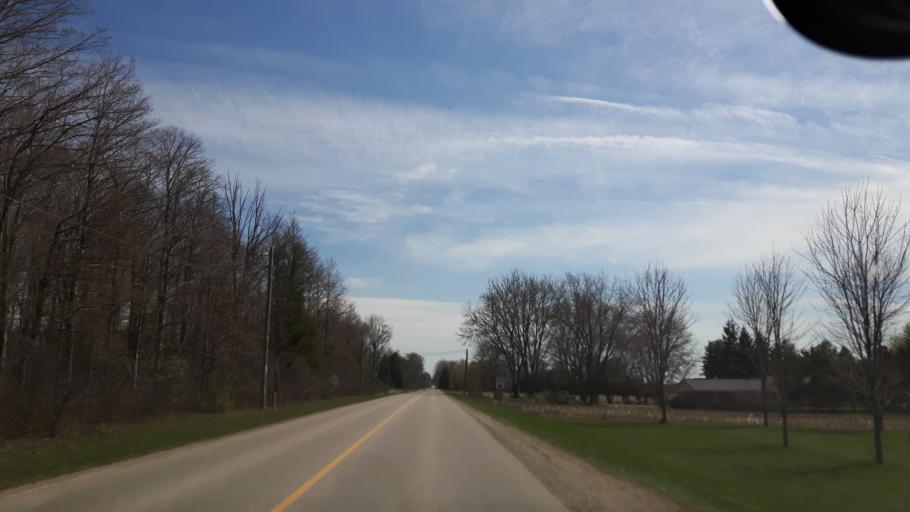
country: CA
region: Ontario
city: Goderich
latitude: 43.7167
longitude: -81.6852
